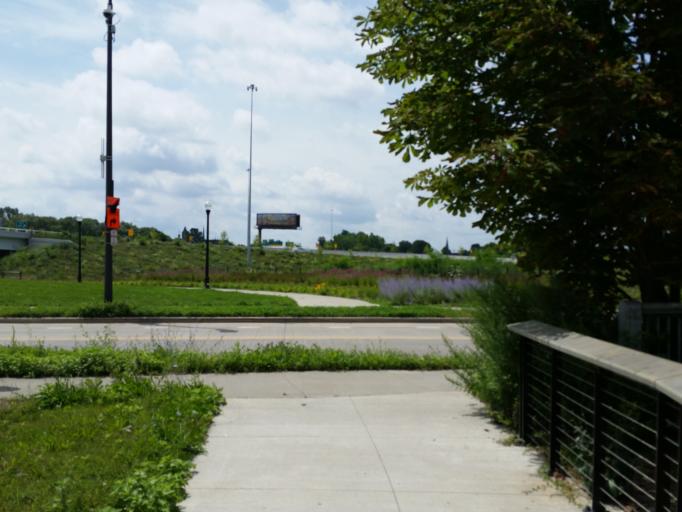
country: US
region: Ohio
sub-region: Cuyahoga County
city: Cleveland
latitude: 41.4845
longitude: -81.6933
